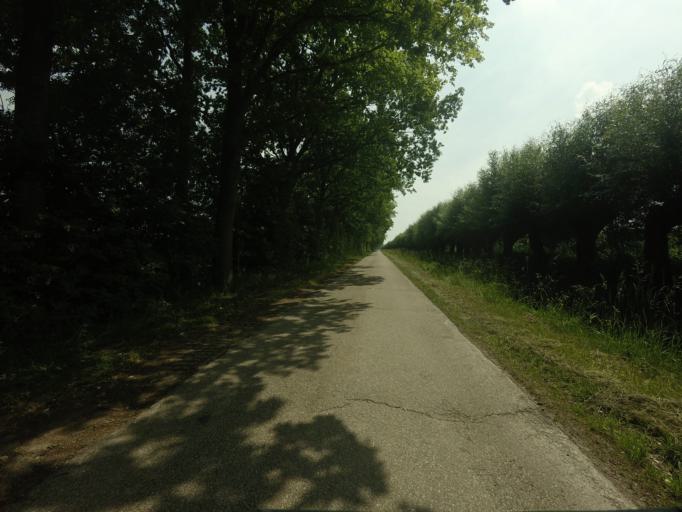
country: NL
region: Gelderland
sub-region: Gemeente Culemborg
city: Culemborg
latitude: 51.9939
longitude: 5.2260
